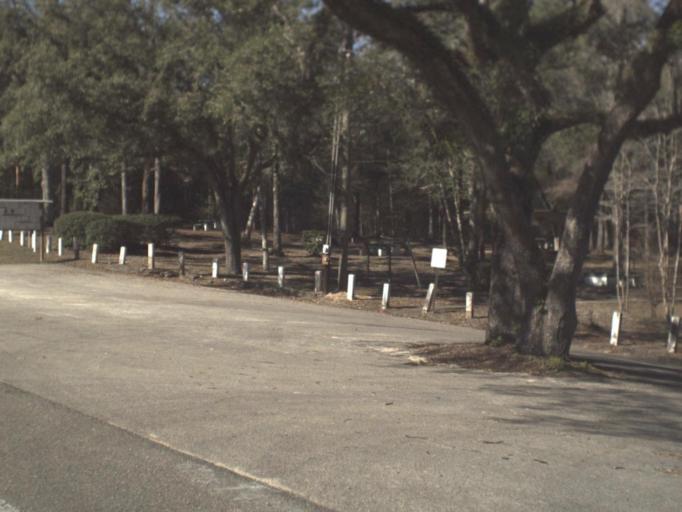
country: US
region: Florida
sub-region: Calhoun County
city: Blountstown
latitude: 30.4316
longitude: -85.1725
